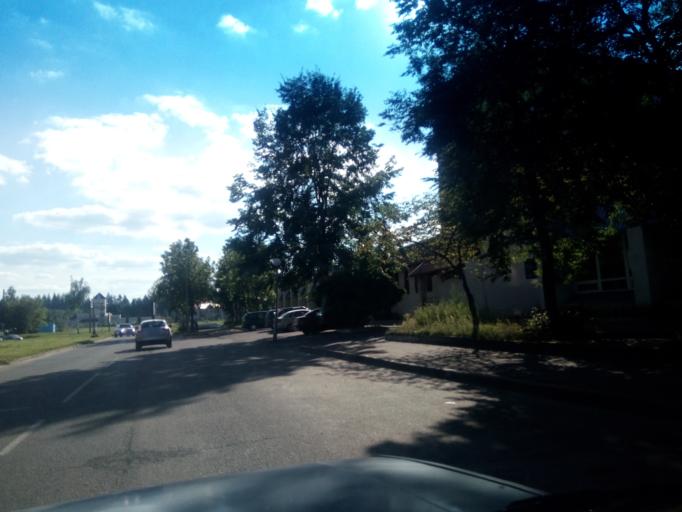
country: BY
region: Vitebsk
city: Navapolatsk
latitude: 55.5232
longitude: 28.6642
